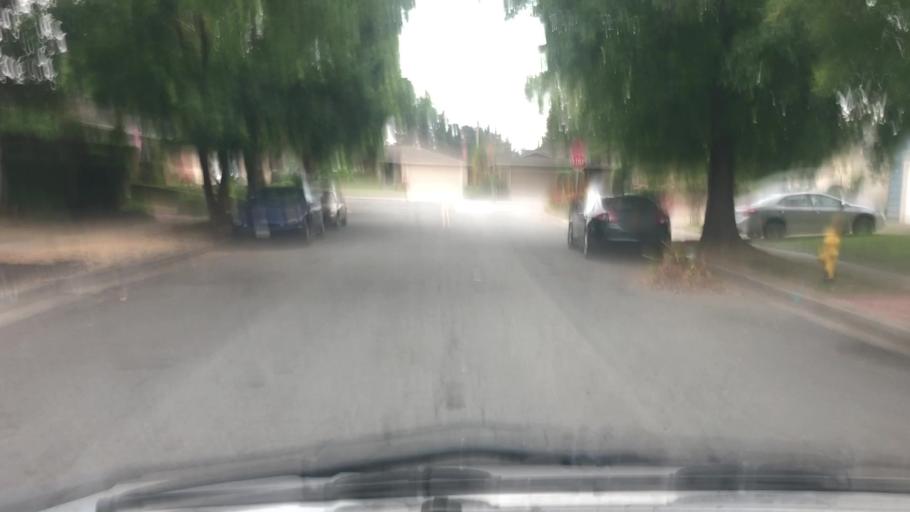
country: US
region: California
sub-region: Santa Clara County
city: Campbell
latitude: 37.3099
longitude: -121.9881
